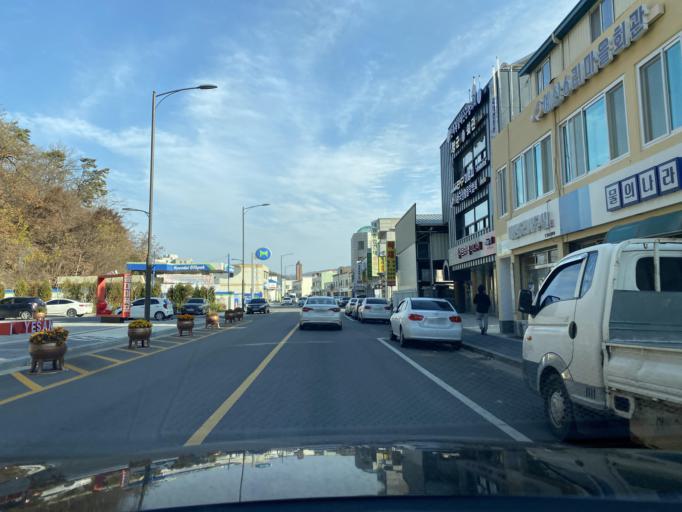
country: KR
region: Chungcheongnam-do
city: Yesan
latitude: 36.6788
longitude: 126.8393
